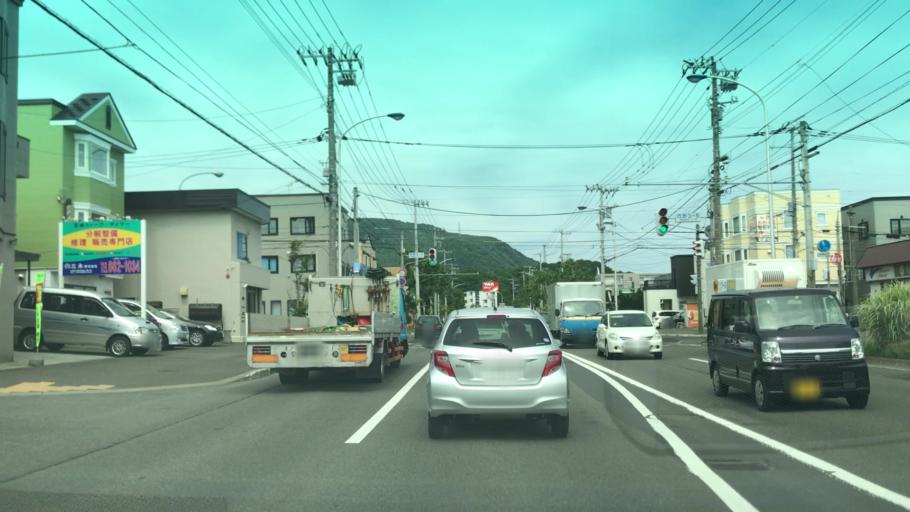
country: JP
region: Hokkaido
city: Sapporo
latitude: 43.0768
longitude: 141.2741
